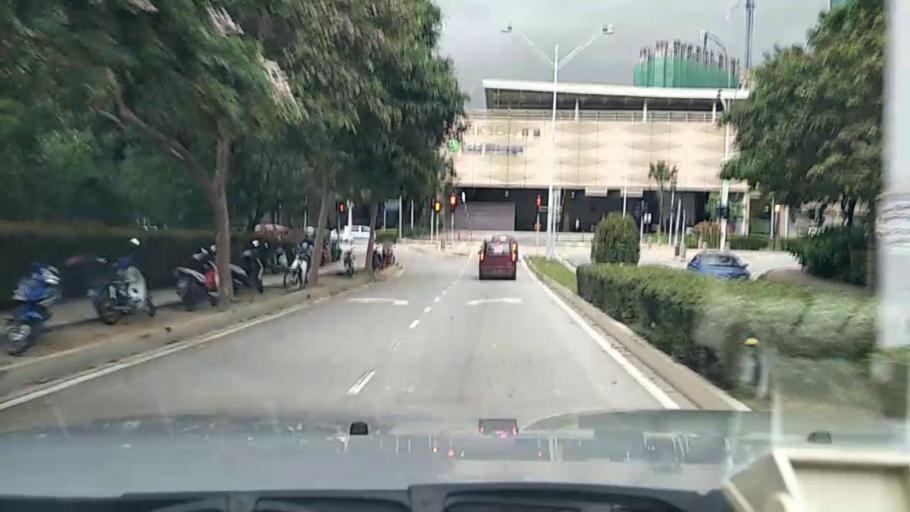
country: MY
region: Putrajaya
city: Putrajaya
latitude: 2.9372
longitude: 101.7110
